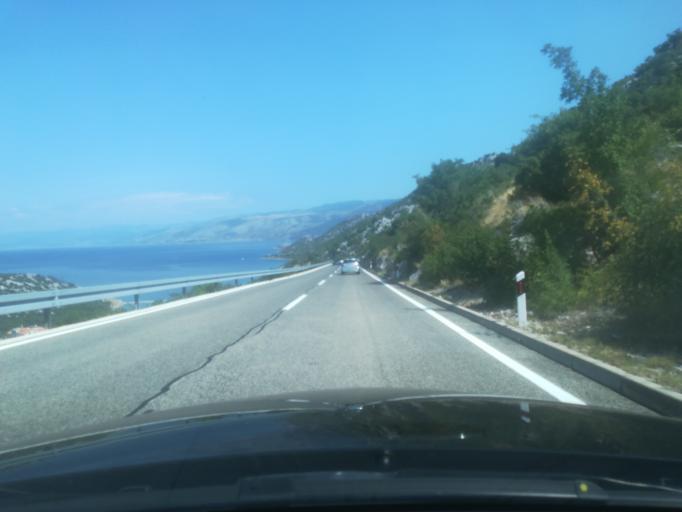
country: HR
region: Licko-Senjska
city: Senj
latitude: 44.8982
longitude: 14.9117
